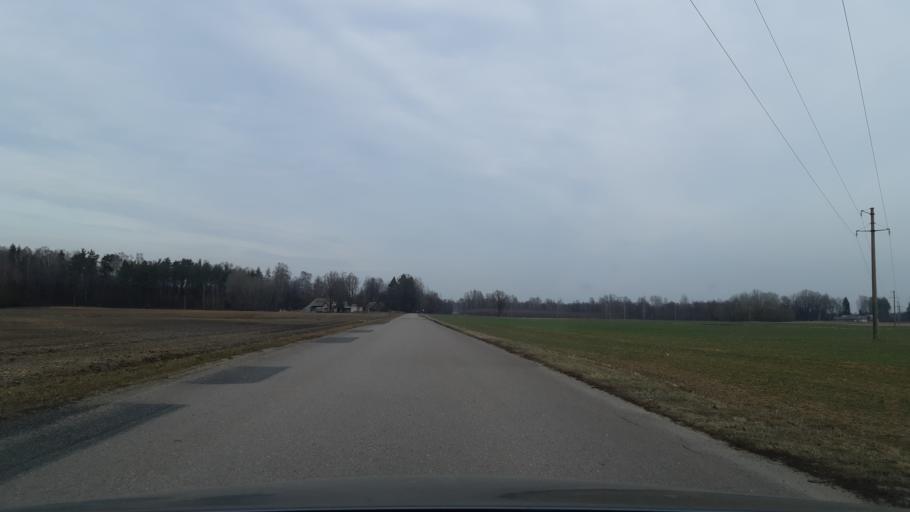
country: LT
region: Marijampoles apskritis
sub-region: Marijampole Municipality
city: Marijampole
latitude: 54.7290
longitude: 23.3374
